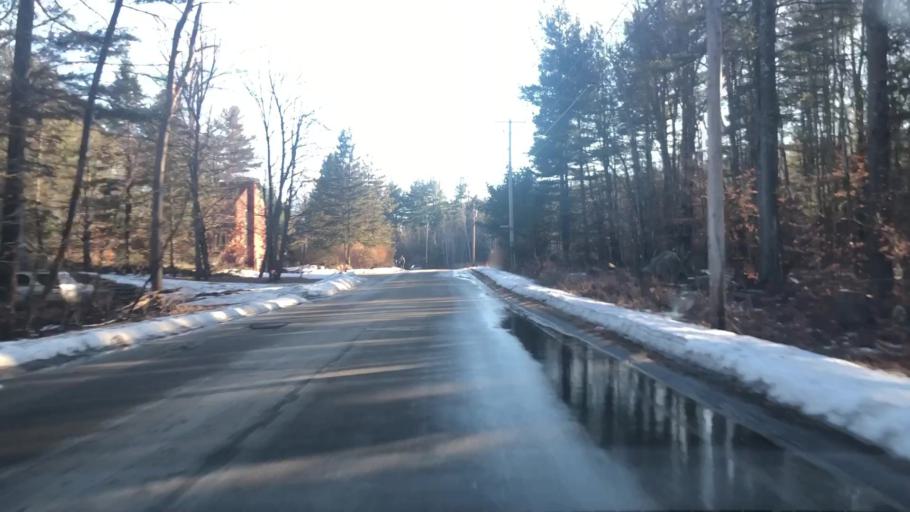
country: US
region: New Hampshire
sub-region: Hillsborough County
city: Milford
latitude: 42.8375
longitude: -71.6811
